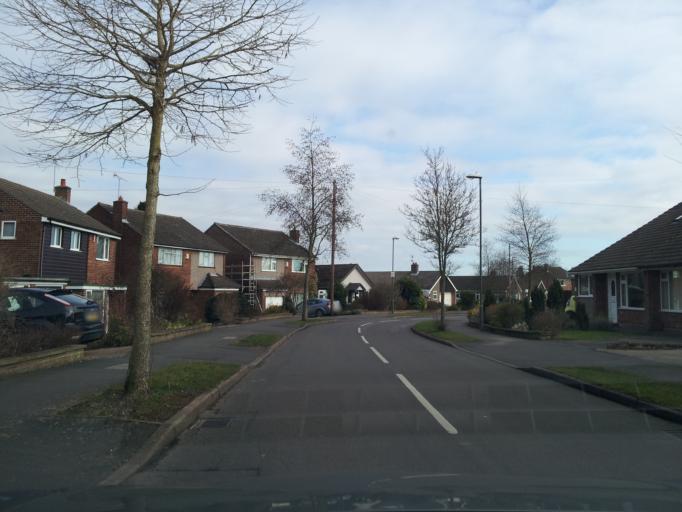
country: GB
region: England
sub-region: Derbyshire
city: Findern
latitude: 52.9186
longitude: -1.5379
